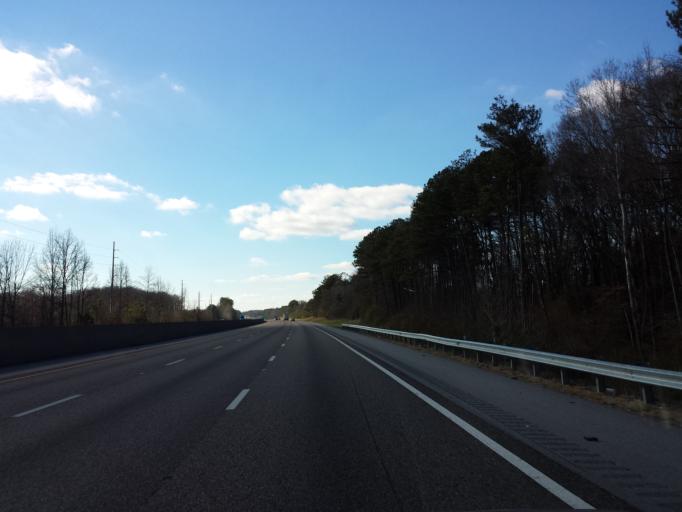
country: US
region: Alabama
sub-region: Calhoun County
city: Oxford
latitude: 33.5855
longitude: -85.8973
